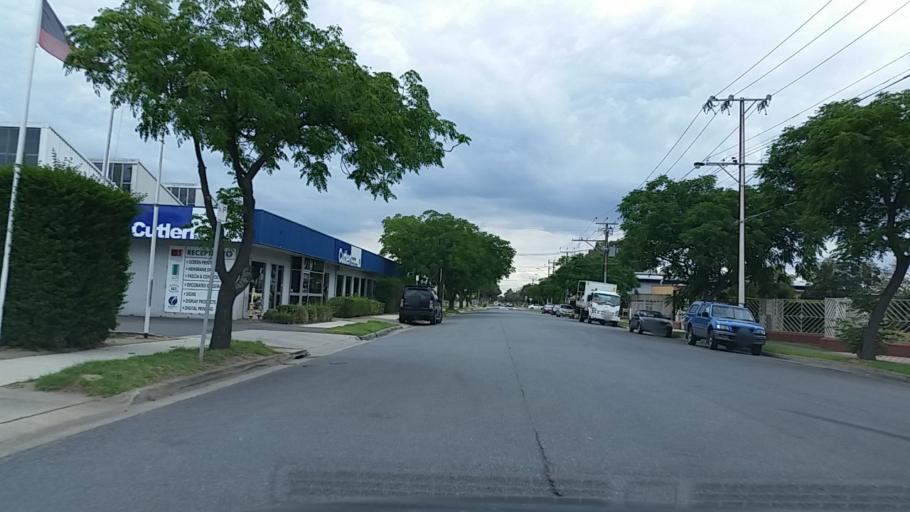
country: AU
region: South Australia
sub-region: Charles Sturt
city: Woodville
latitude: -34.8736
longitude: 138.5546
